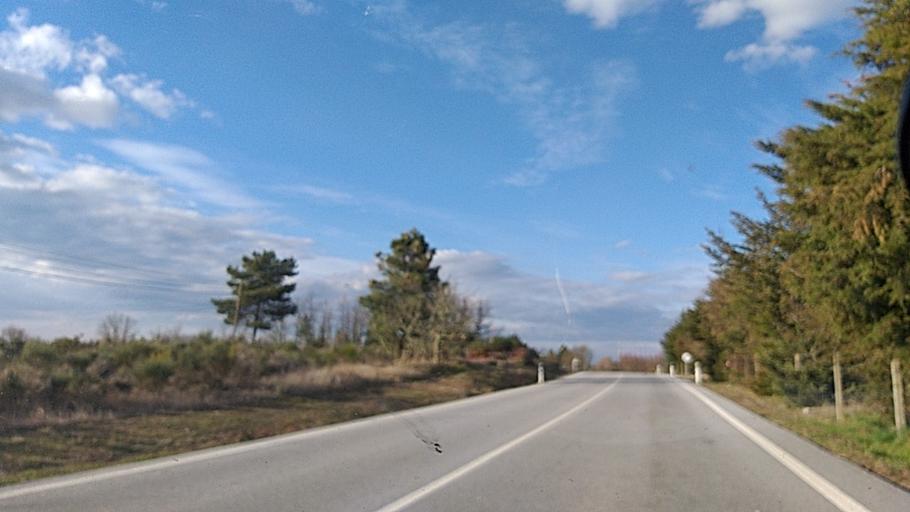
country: ES
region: Castille and Leon
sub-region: Provincia de Salamanca
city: Fuentes de Onoro
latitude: 40.6415
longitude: -6.8561
